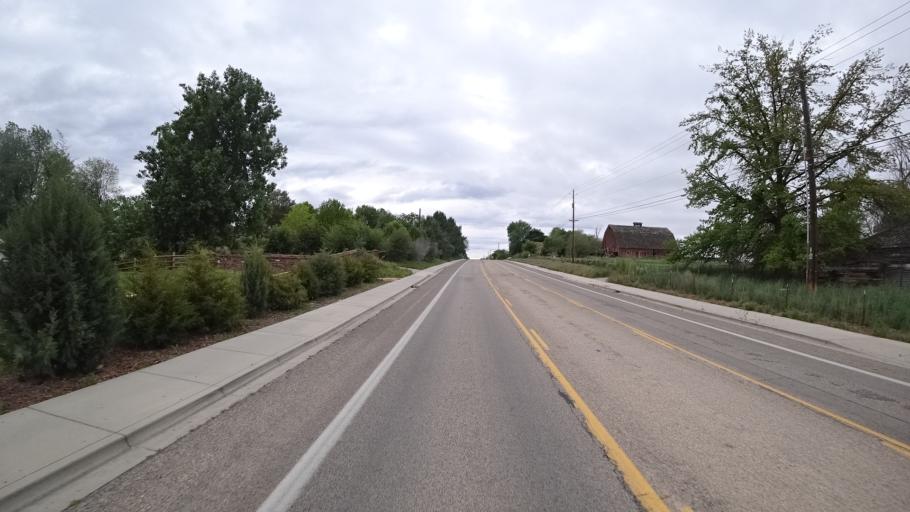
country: US
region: Idaho
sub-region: Ada County
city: Eagle
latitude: 43.7064
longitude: -116.3587
